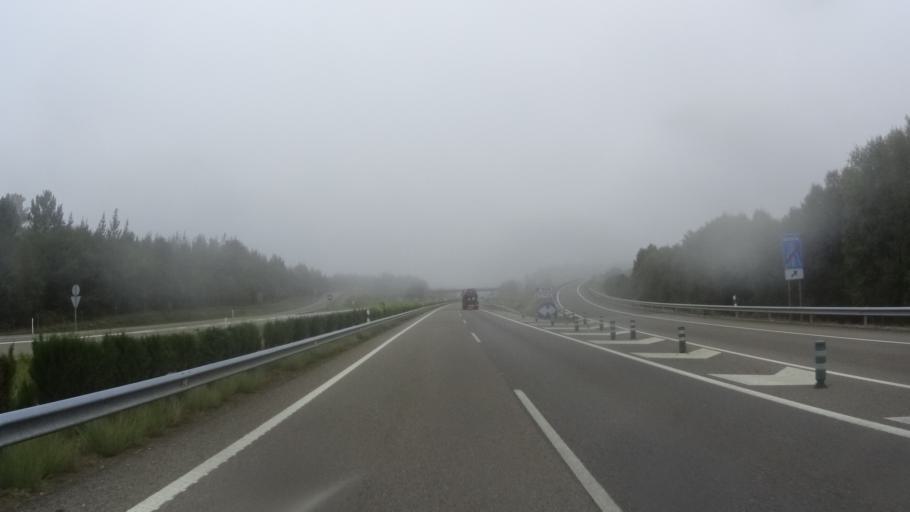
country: ES
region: Galicia
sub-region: Provincia de Lugo
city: Guitiriz
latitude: 43.1833
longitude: -7.8204
